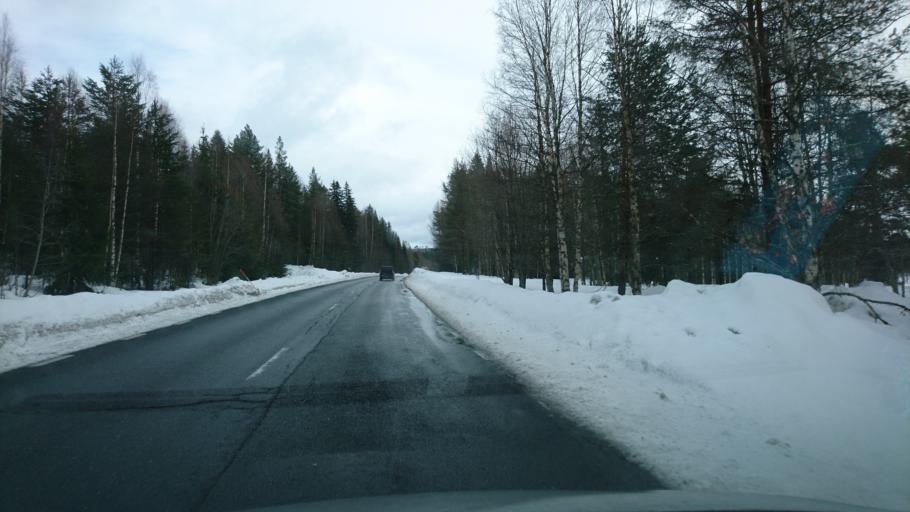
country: SE
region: Vaesternorrland
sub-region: Solleftea Kommun
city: Solleftea
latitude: 63.0452
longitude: 17.0693
